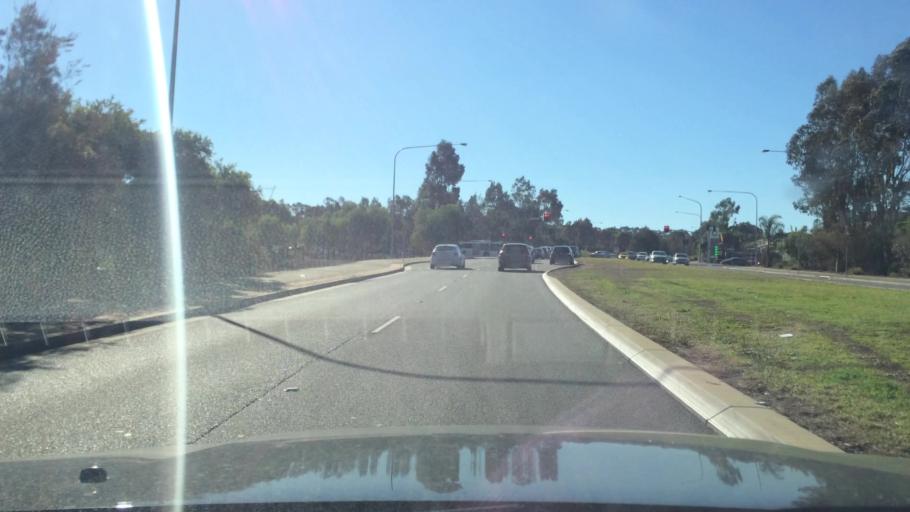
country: AU
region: New South Wales
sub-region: Fairfield
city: Cecil Park
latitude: -33.8958
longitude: 150.8565
